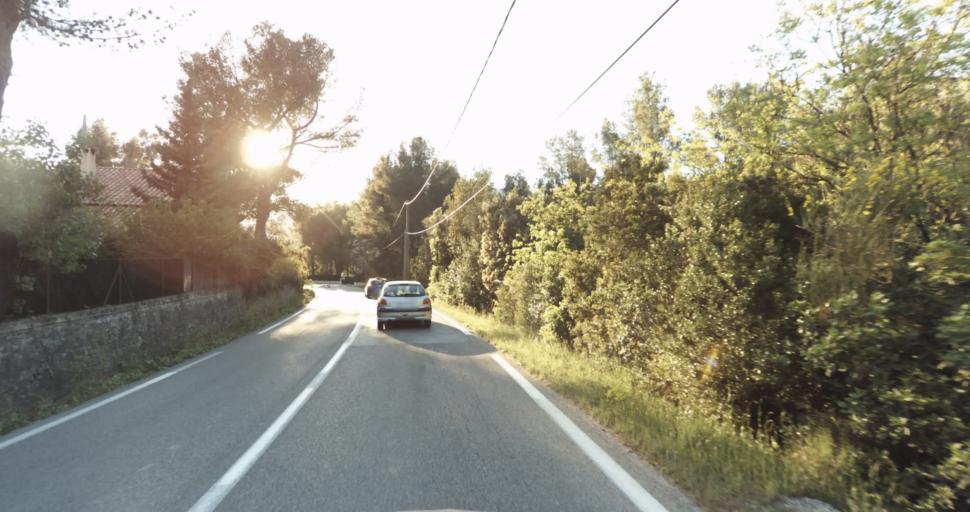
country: FR
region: Provence-Alpes-Cote d'Azur
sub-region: Departement du Var
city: Le Revest-les-Eaux
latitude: 43.1622
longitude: 5.9508
